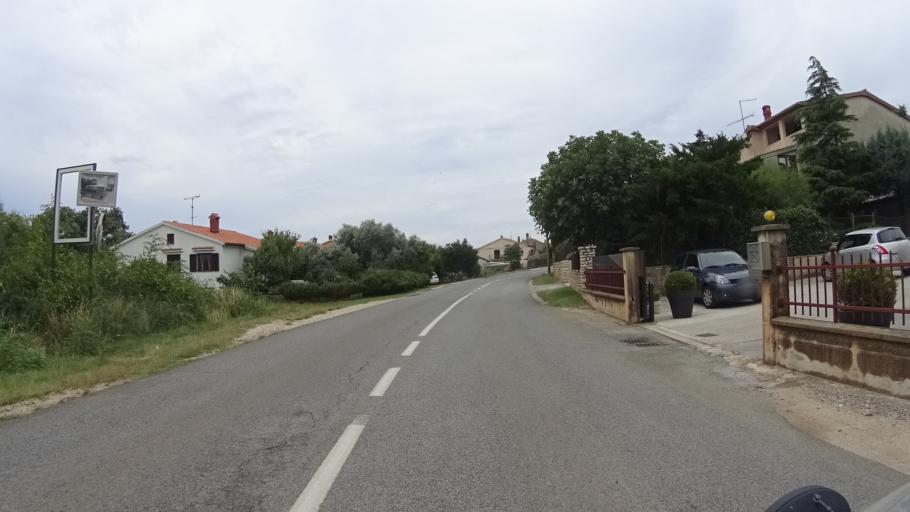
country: HR
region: Istarska
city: Medulin
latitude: 44.8596
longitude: 13.9019
